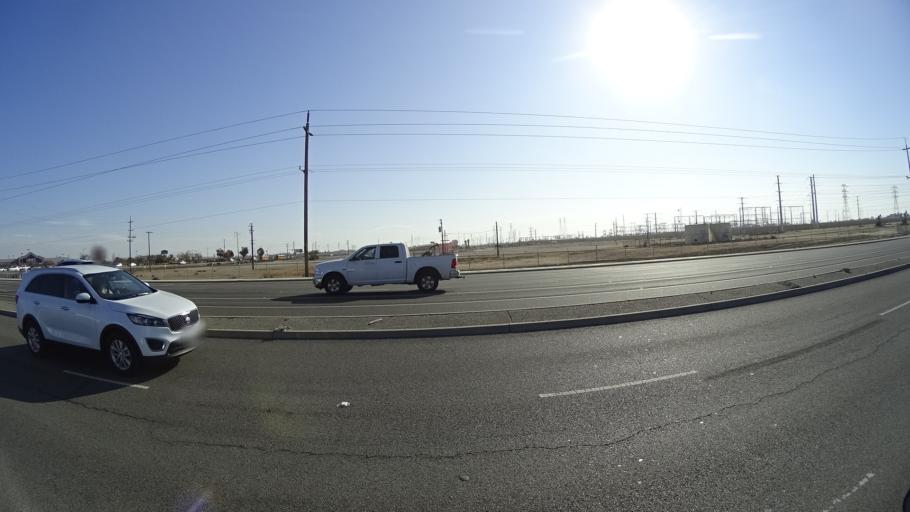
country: US
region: California
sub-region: Kern County
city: Greenacres
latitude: 35.3836
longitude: -119.0942
